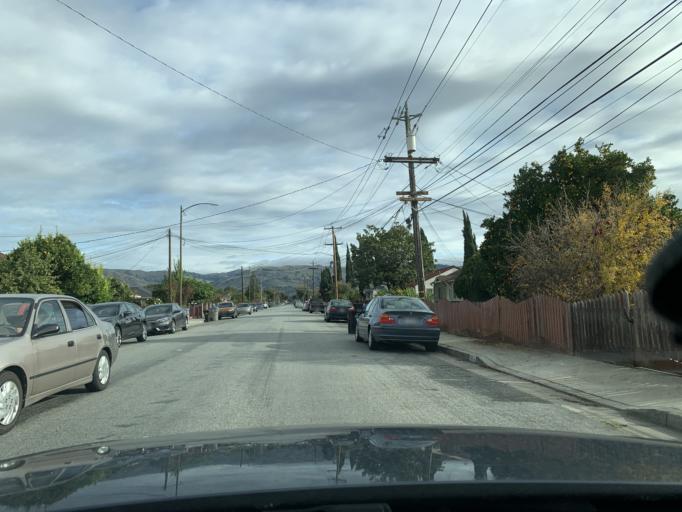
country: US
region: California
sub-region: Santa Clara County
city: Alum Rock
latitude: 37.3473
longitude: -121.8493
